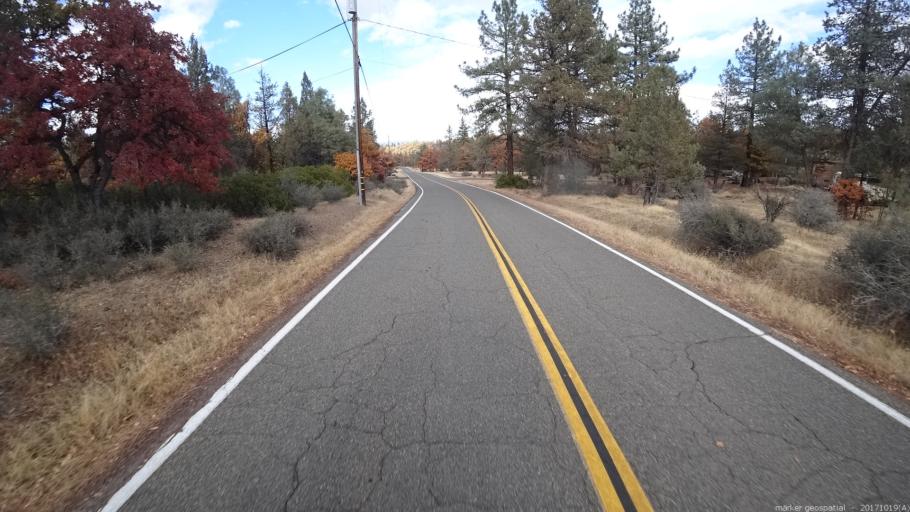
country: US
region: California
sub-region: Shasta County
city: Burney
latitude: 40.9673
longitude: -121.4351
